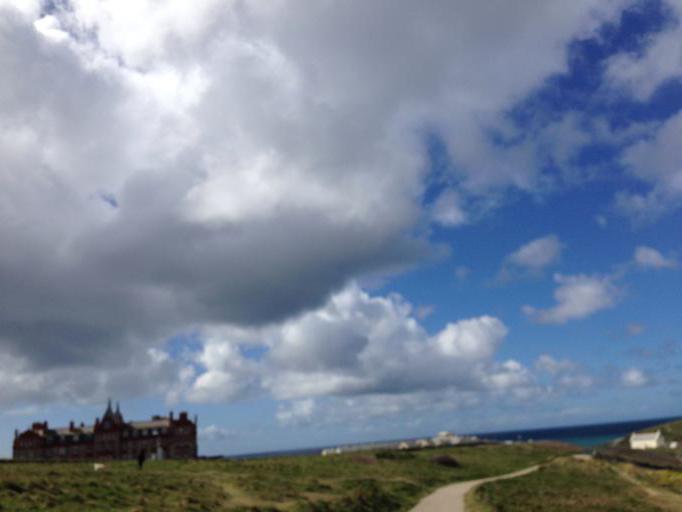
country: GB
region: England
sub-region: Cornwall
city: Newquay
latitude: 50.4203
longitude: -5.0939
